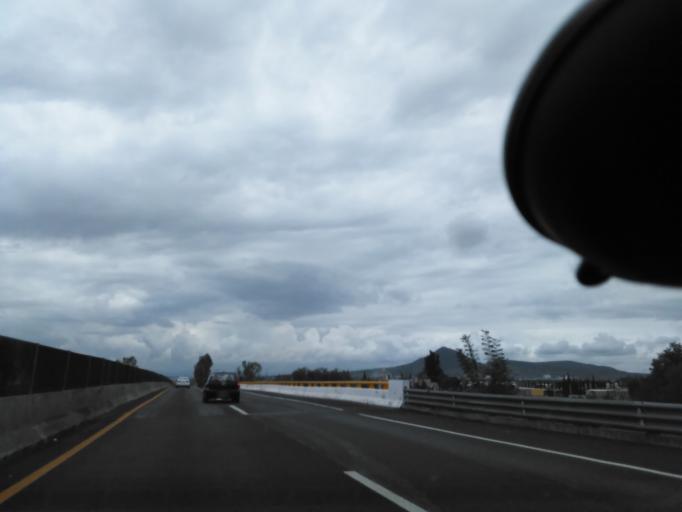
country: MX
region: Mexico
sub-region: Huehuetoca
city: Casa Nueva
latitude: 19.8196
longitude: -99.2036
